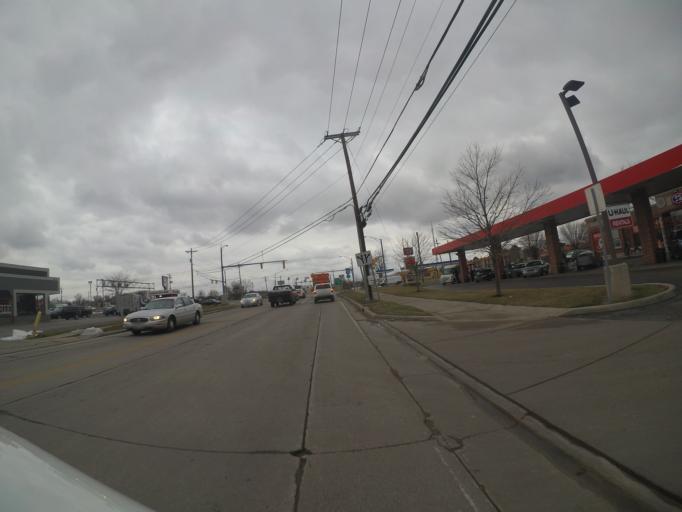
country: US
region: Ohio
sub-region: Wood County
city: Rossford
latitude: 41.6090
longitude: -83.5373
